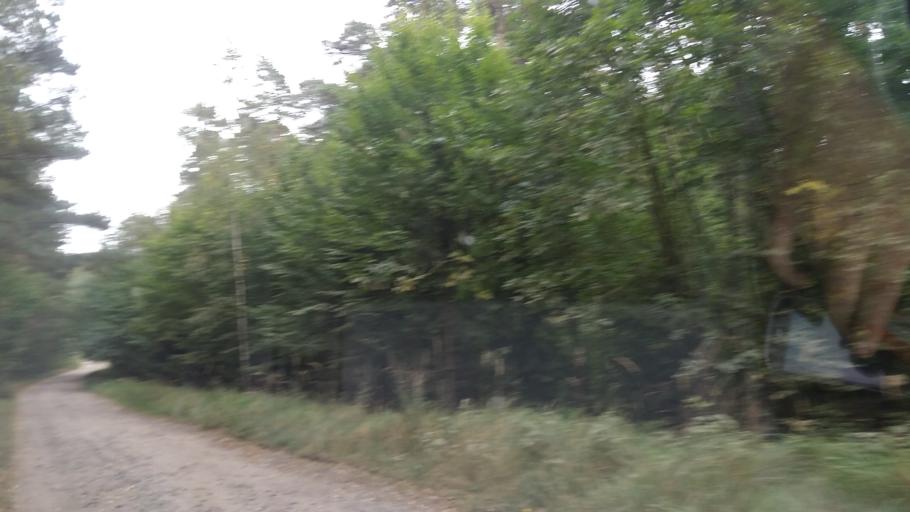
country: PL
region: West Pomeranian Voivodeship
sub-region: Powiat choszczenski
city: Bierzwnik
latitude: 52.9758
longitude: 15.6107
